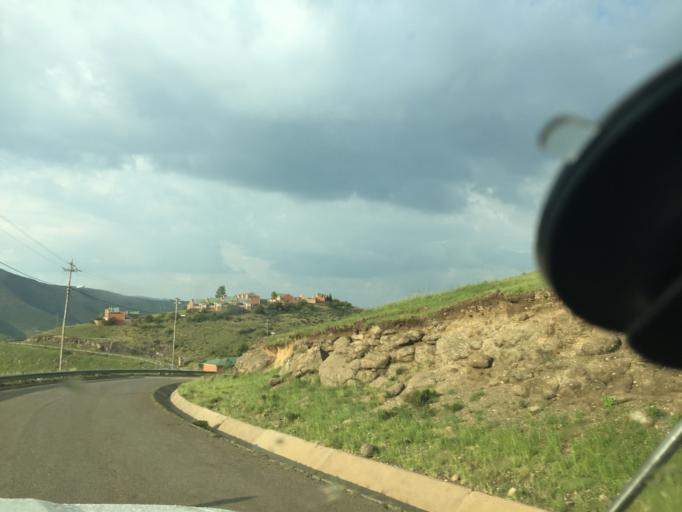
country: LS
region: Maseru
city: Nako
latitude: -29.4796
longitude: 28.0579
